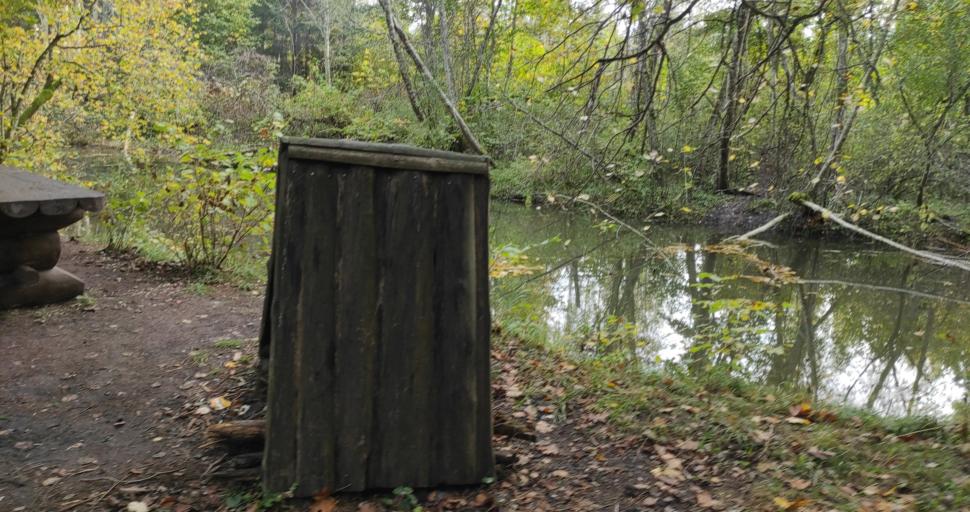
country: LV
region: Jaunpils
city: Jaunpils
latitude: 56.8144
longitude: 22.9567
